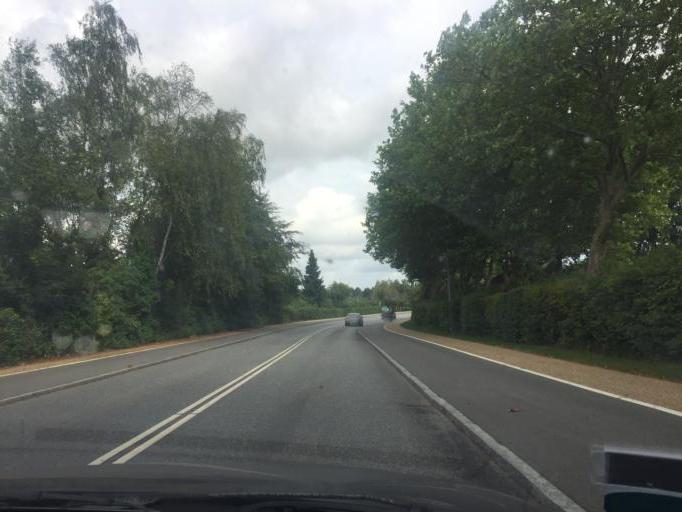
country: DK
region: Capital Region
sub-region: Allerod Kommune
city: Lillerod
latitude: 55.8779
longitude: 12.3513
